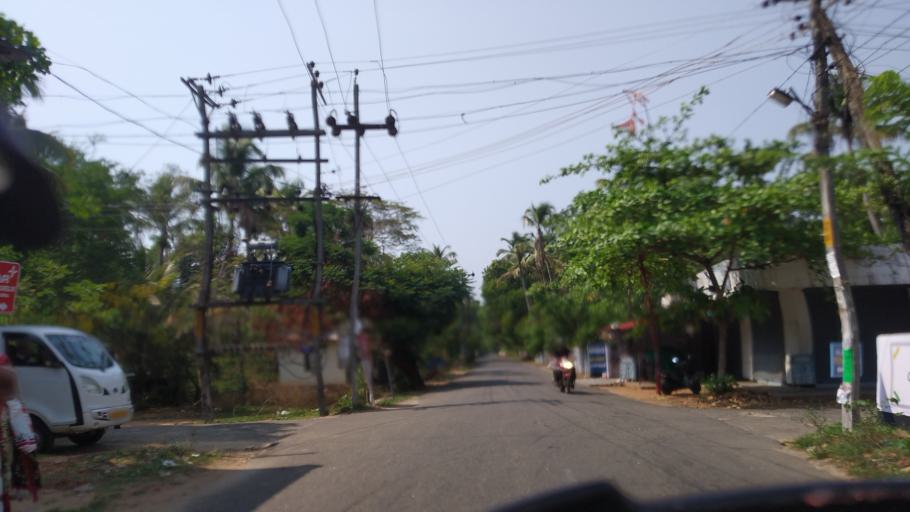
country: IN
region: Kerala
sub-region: Thrissur District
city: Irinjalakuda
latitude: 10.3131
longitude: 76.1269
